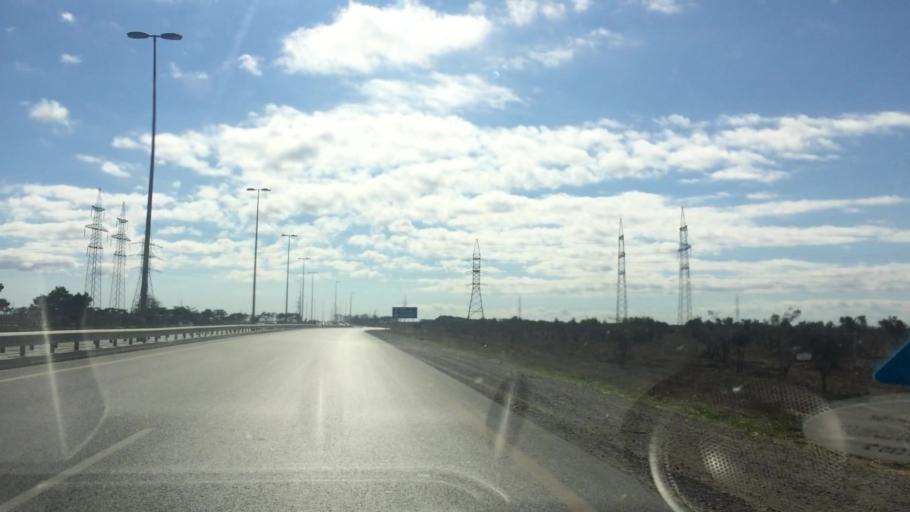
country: AZ
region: Baki
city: Qala
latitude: 40.4387
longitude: 50.1827
